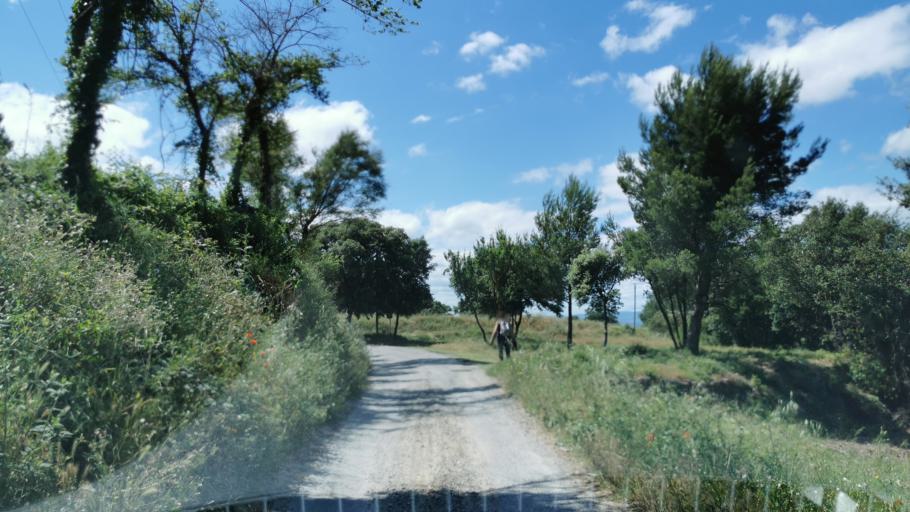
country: FR
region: Languedoc-Roussillon
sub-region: Departement de l'Aude
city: Moussan
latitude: 43.2344
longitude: 2.9400
